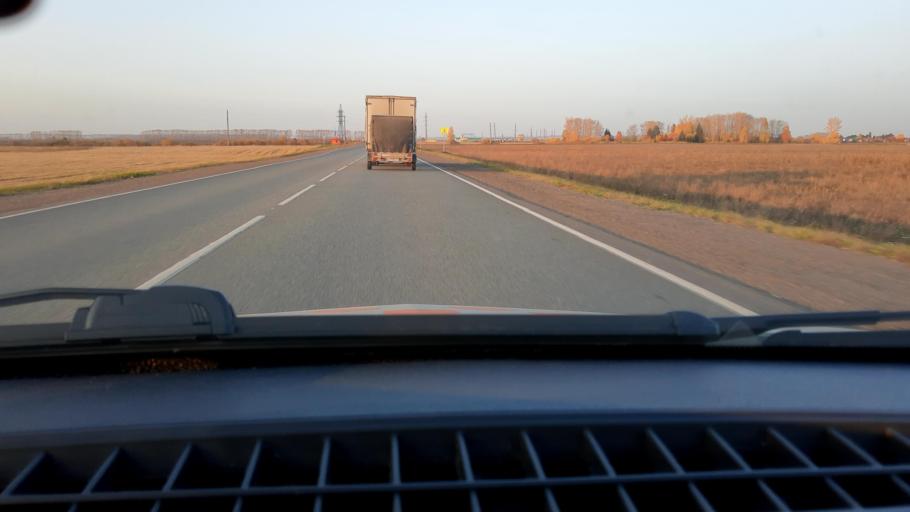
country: RU
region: Bashkortostan
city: Mikhaylovka
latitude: 54.9432
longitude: 55.7492
